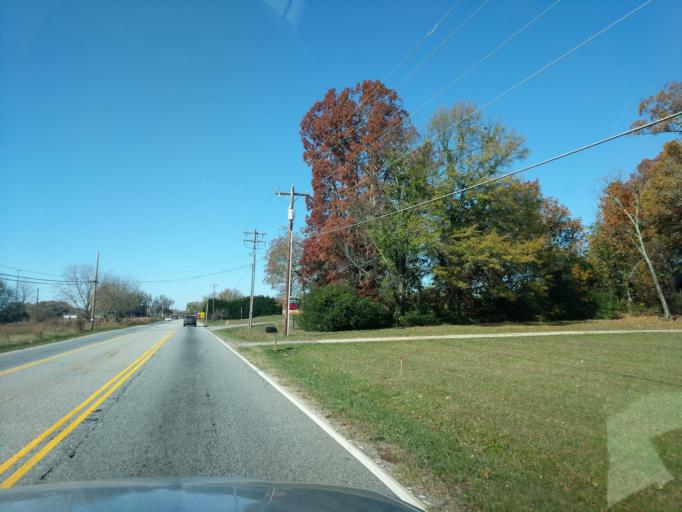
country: US
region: South Carolina
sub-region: Greenville County
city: Taylors
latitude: 34.9578
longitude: -82.3016
